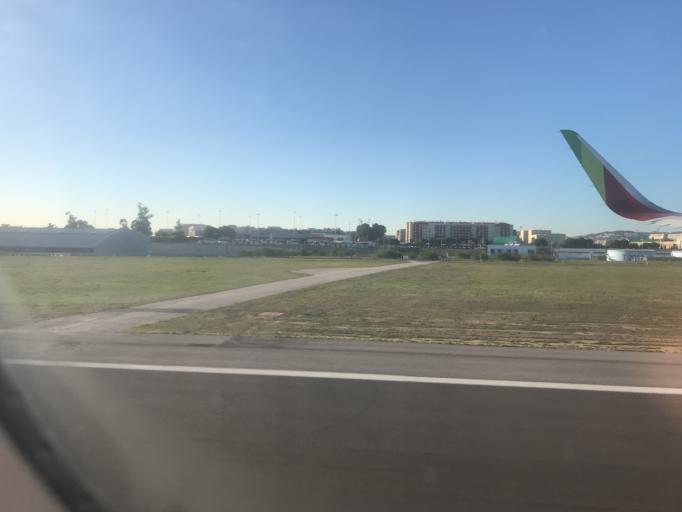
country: PT
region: Lisbon
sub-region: Odivelas
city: Olival do Basto
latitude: 38.7713
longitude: -9.1415
